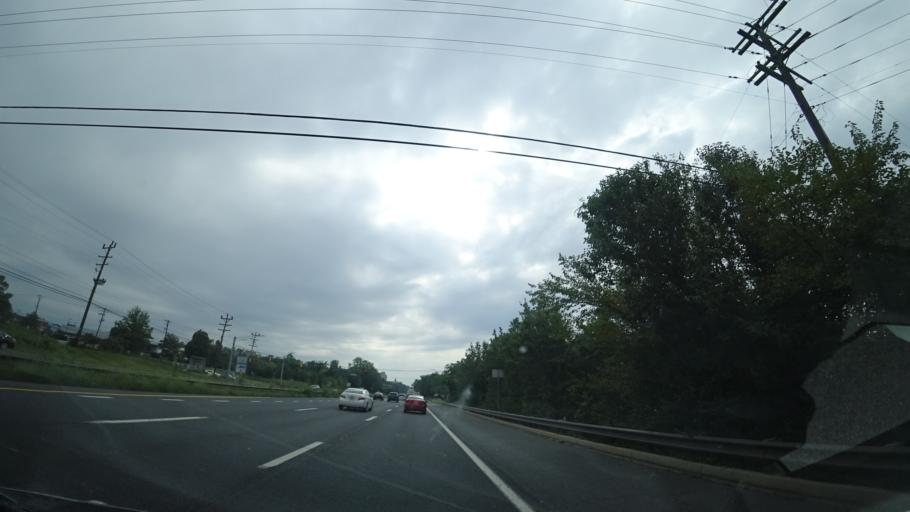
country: US
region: Maryland
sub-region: Montgomery County
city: Fairland
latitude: 39.0569
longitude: -76.9705
